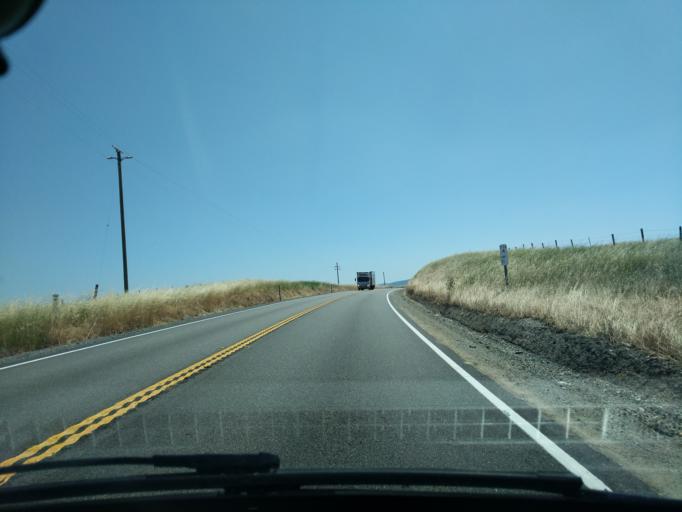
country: US
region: California
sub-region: Stanislaus County
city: East Oakdale
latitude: 37.9447
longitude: -120.8264
